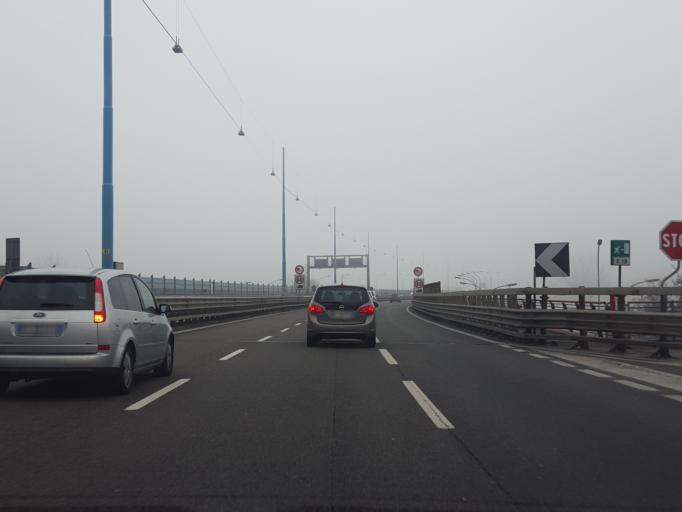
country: IT
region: Veneto
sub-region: Provincia di Venezia
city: Mestre
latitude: 45.4887
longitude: 12.2205
